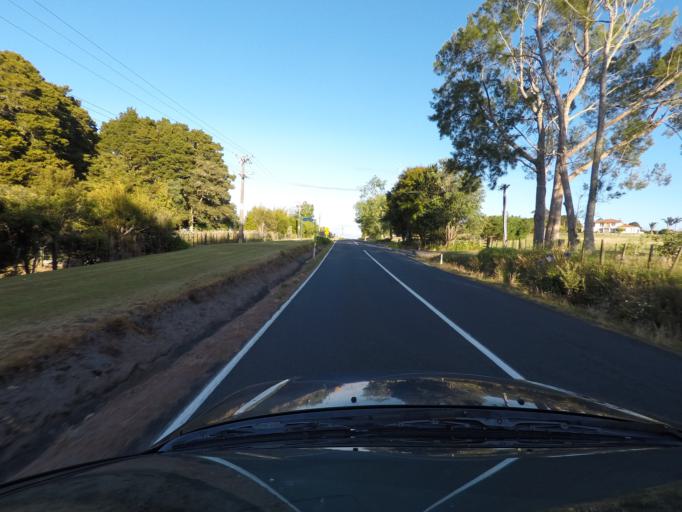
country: NZ
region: Northland
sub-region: Whangarei
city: Whangarei
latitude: -35.6592
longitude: 174.3146
